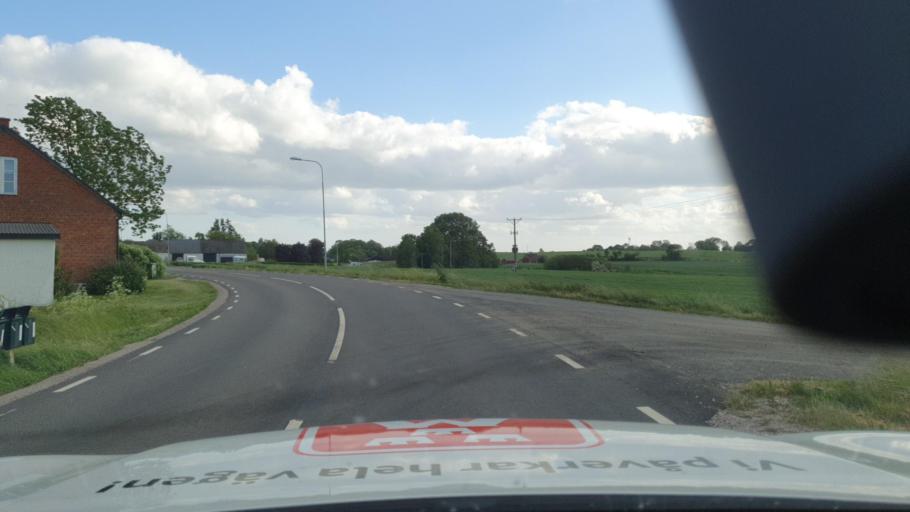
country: SE
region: Skane
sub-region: Tomelilla Kommun
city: Tomelilla
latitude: 55.5863
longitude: 14.0170
